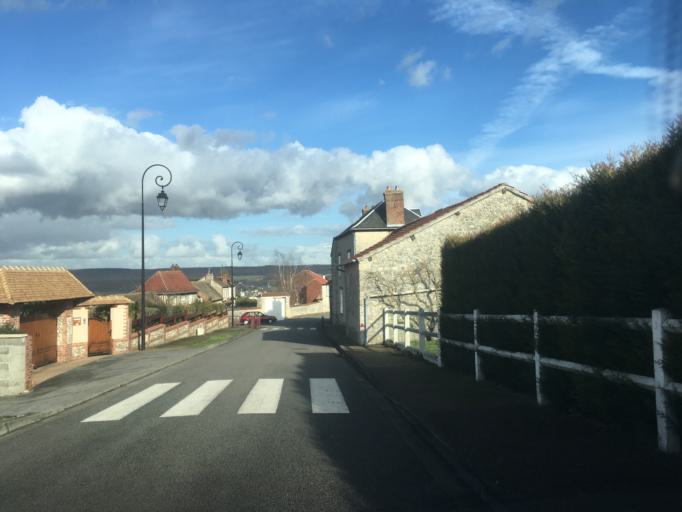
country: FR
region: Haute-Normandie
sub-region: Departement de l'Eure
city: Saint-Marcel
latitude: 49.0918
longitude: 1.4458
